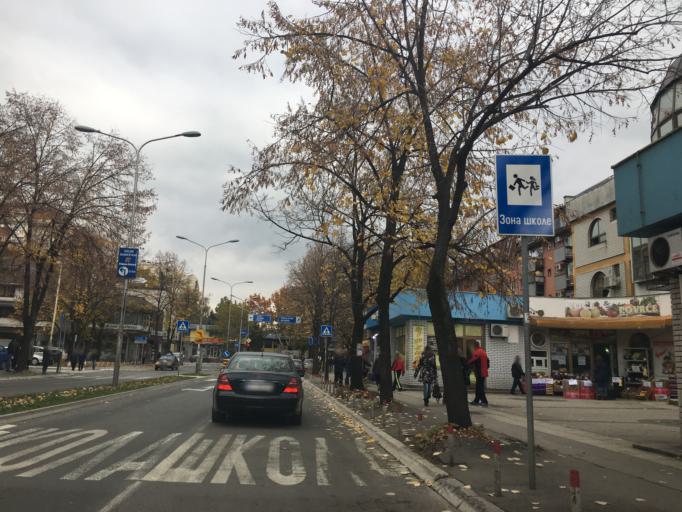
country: RS
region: Central Serbia
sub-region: Raski Okrug
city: Kraljevo
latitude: 43.7246
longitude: 20.6952
